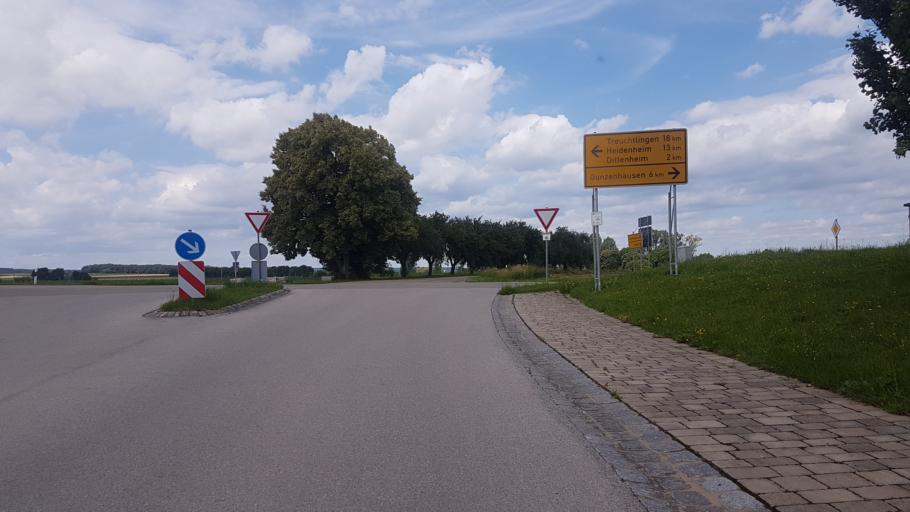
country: DE
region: Bavaria
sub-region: Regierungsbezirk Mittelfranken
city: Dittenheim
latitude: 49.0775
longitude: 10.7942
